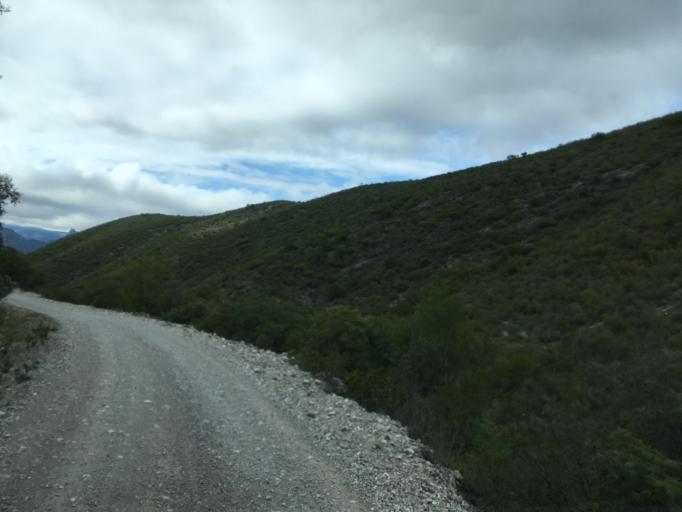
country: MX
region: Hidalgo
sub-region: Metztitlan
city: Fontezuelas
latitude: 20.6228
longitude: -98.8721
